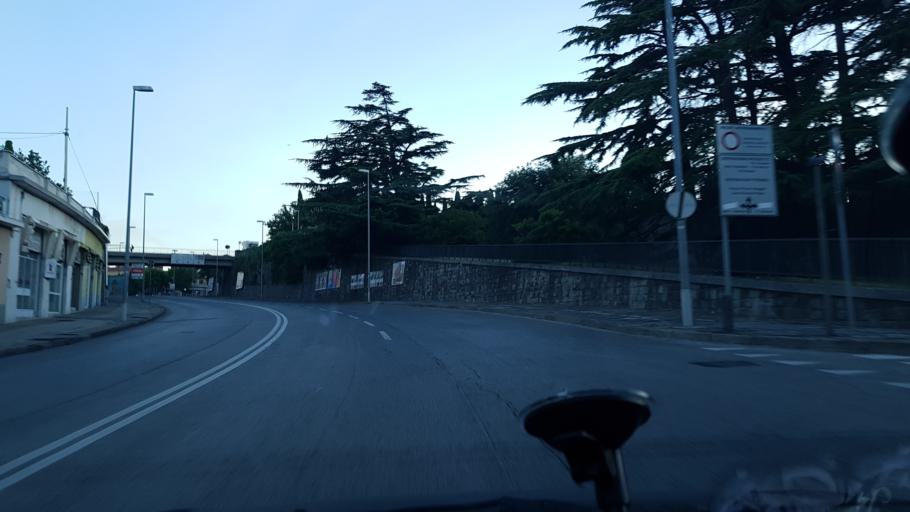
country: IT
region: Friuli Venezia Giulia
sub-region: Provincia di Trieste
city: Trieste
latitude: 45.6297
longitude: 13.7936
